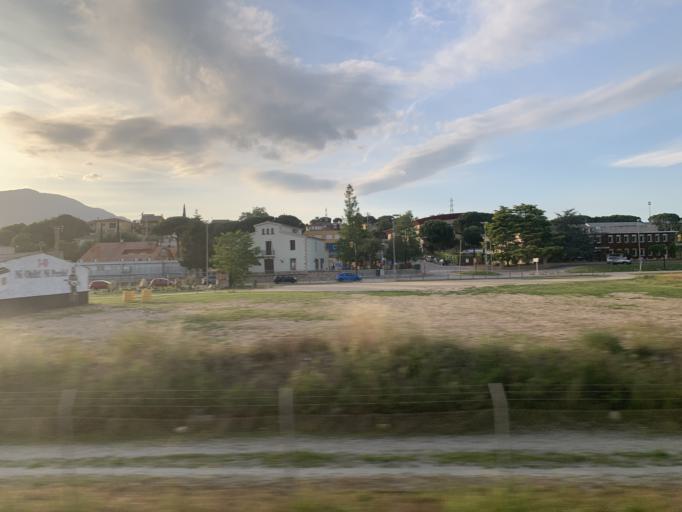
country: ES
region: Catalonia
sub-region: Provincia de Girona
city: Breda
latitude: 41.7241
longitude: 2.5587
